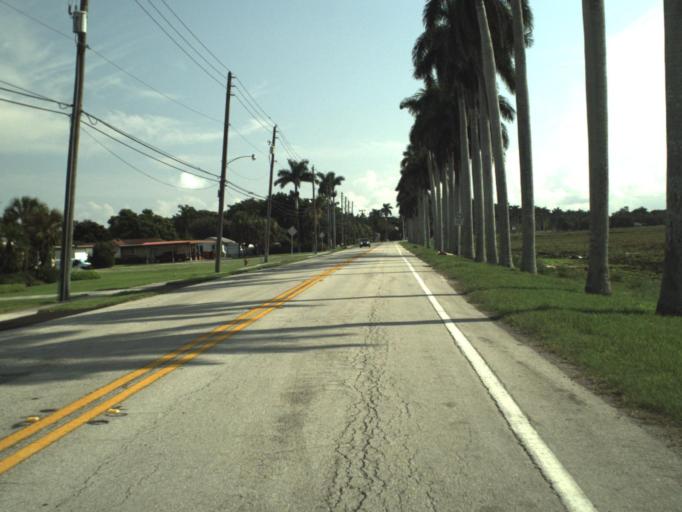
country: US
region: Florida
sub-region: Palm Beach County
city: Pahokee
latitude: 26.8057
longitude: -80.6922
